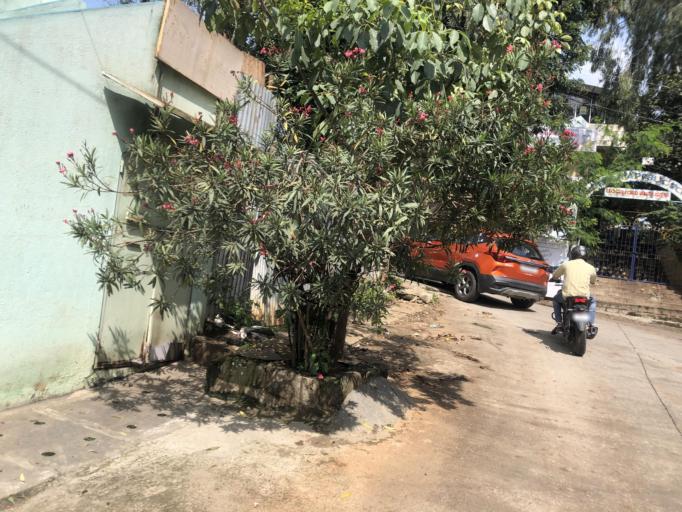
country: IN
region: Karnataka
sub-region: Bangalore Urban
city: Bangalore
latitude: 12.9215
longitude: 77.5287
